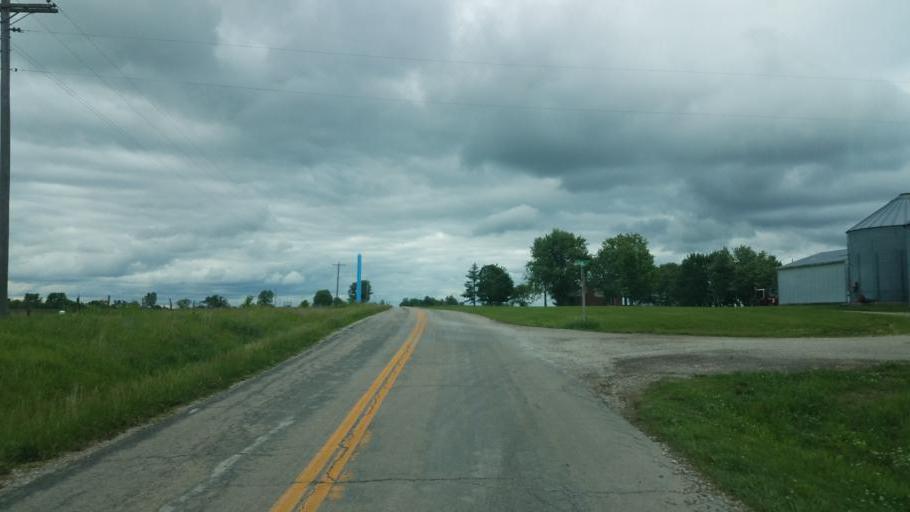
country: US
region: Missouri
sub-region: Mercer County
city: Princeton
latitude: 40.3729
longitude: -93.6801
